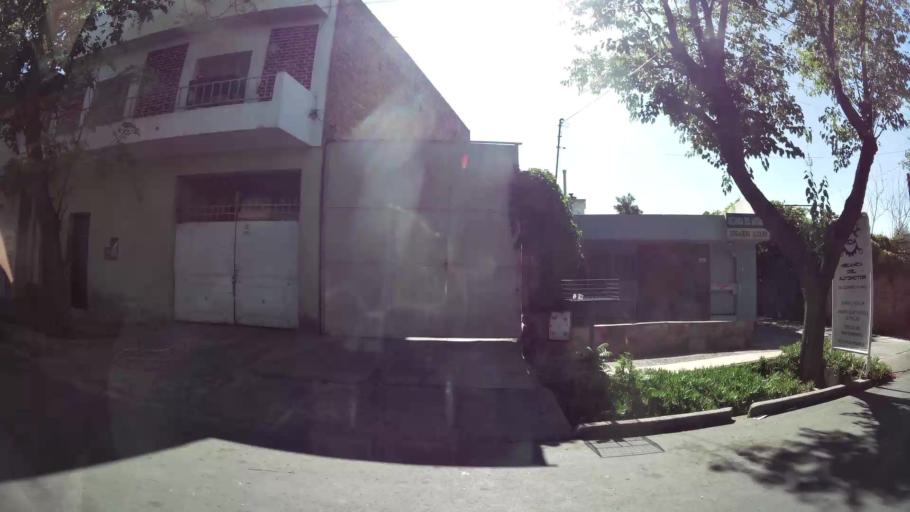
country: AR
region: Mendoza
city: Villa Nueva
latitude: -32.9020
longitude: -68.7896
